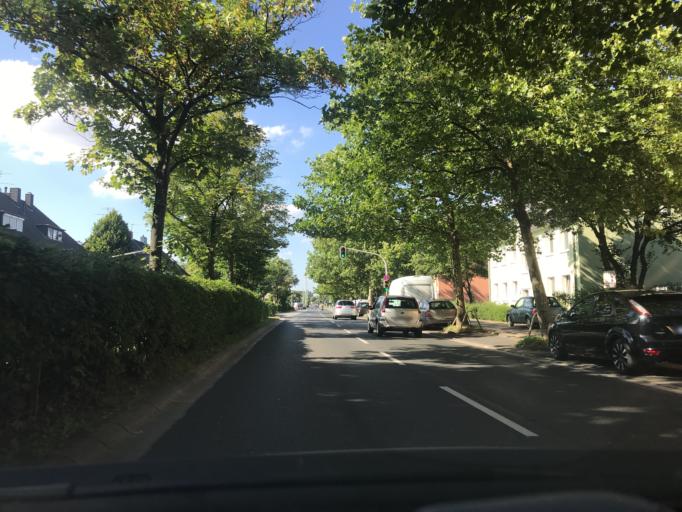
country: DE
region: North Rhine-Westphalia
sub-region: Regierungsbezirk Dusseldorf
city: Neuss
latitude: 51.1706
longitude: 6.6857
